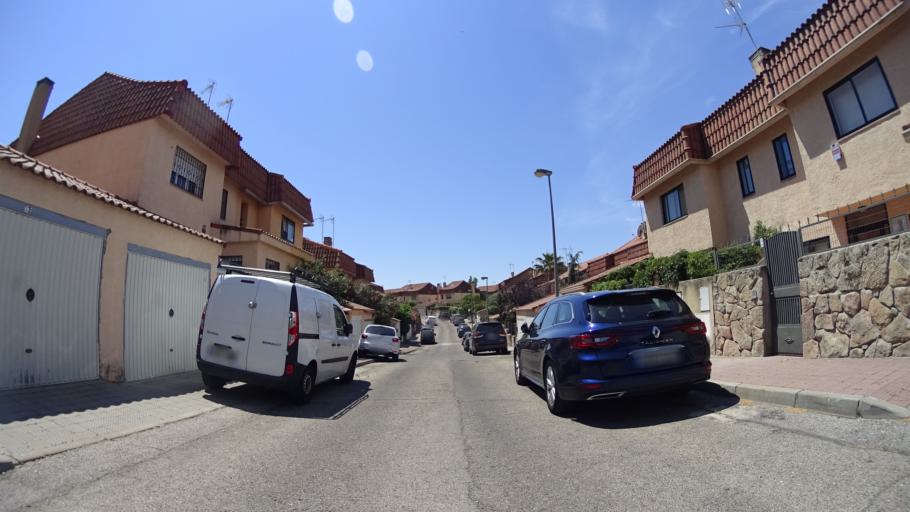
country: ES
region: Madrid
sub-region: Provincia de Madrid
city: Colmenarejo
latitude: 40.5478
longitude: -4.0143
